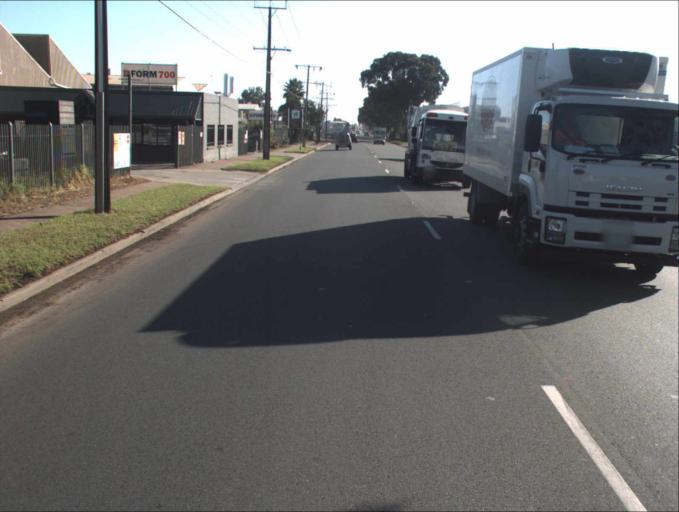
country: AU
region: South Australia
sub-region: Charles Sturt
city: Woodville North
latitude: -34.8445
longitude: 138.5463
